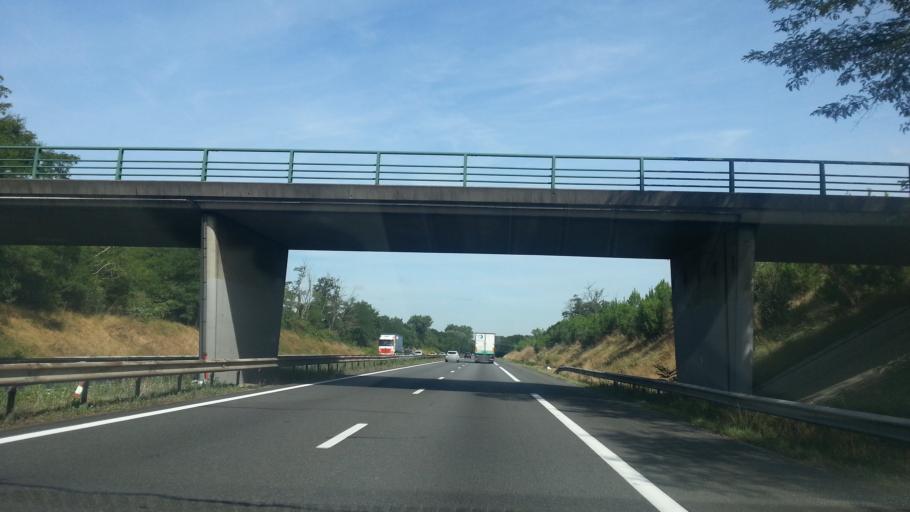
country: FR
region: Aquitaine
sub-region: Departement de la Gironde
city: Cadaujac
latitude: 44.7517
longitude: -0.5421
